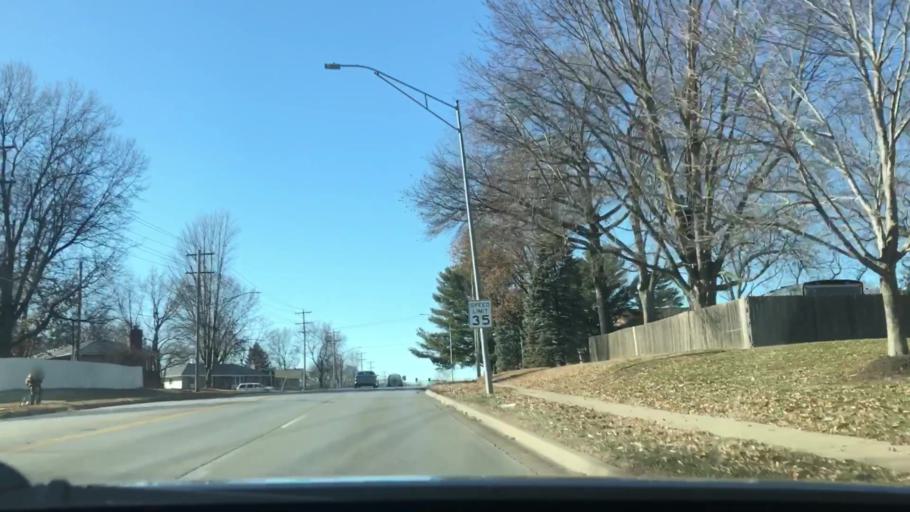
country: US
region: Missouri
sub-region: Jackson County
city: East Independence
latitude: 39.0486
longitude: -94.3737
